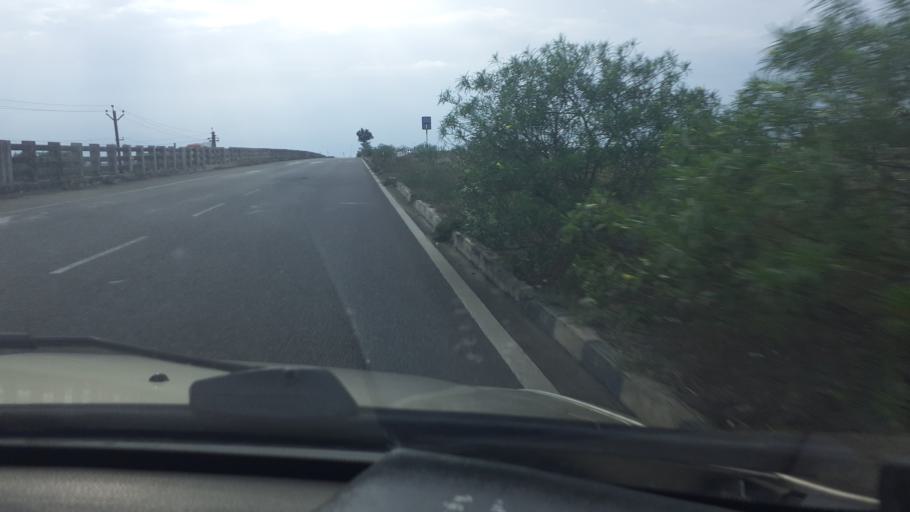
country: IN
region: Tamil Nadu
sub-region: Tirunelveli Kattabo
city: Tirunelveli
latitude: 8.6664
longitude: 77.7406
